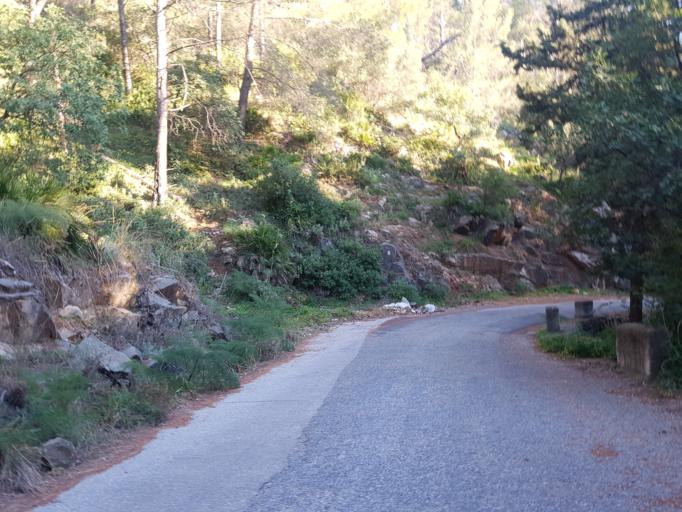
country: ES
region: Andalusia
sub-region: Provincia de Malaga
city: Marbella
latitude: 36.5330
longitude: -4.8840
